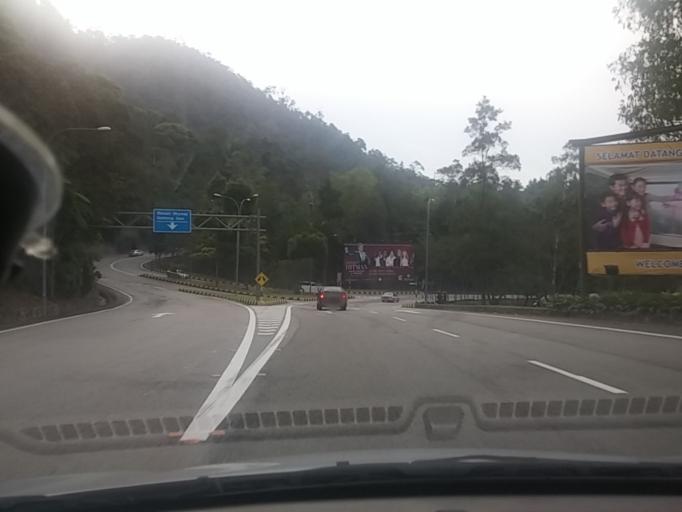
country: MY
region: Pahang
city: Kampung Bukit Tinggi, Bentong
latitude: 3.3817
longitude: 101.7729
